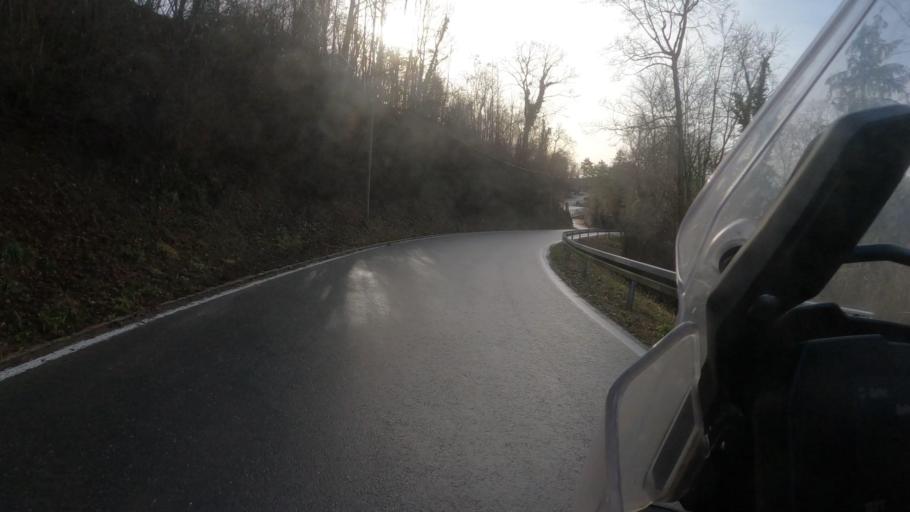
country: DE
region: Baden-Wuerttemberg
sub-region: Freiburg Region
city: Tengen
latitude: 47.8119
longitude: 8.6602
